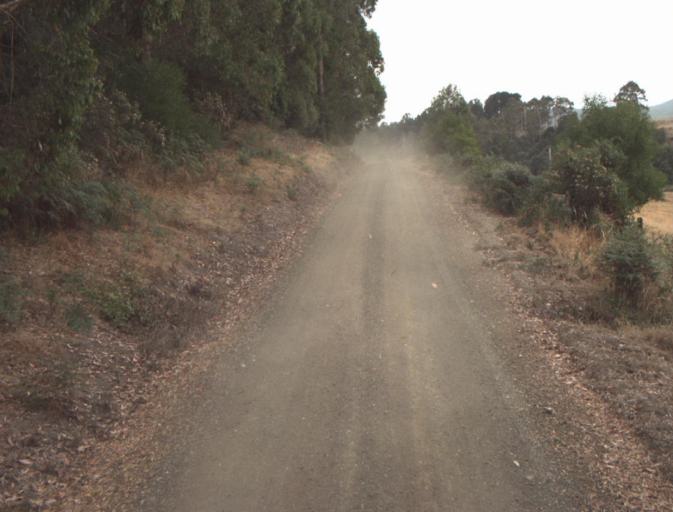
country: AU
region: Tasmania
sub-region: Launceston
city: Mayfield
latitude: -41.1631
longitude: 147.2113
